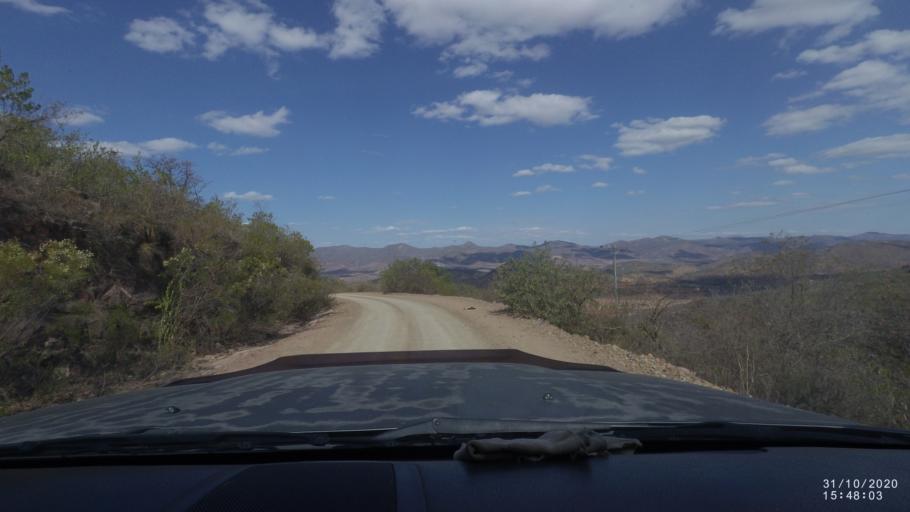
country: BO
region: Chuquisaca
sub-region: Provincia Zudanez
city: Mojocoya
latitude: -18.3136
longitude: -64.7124
